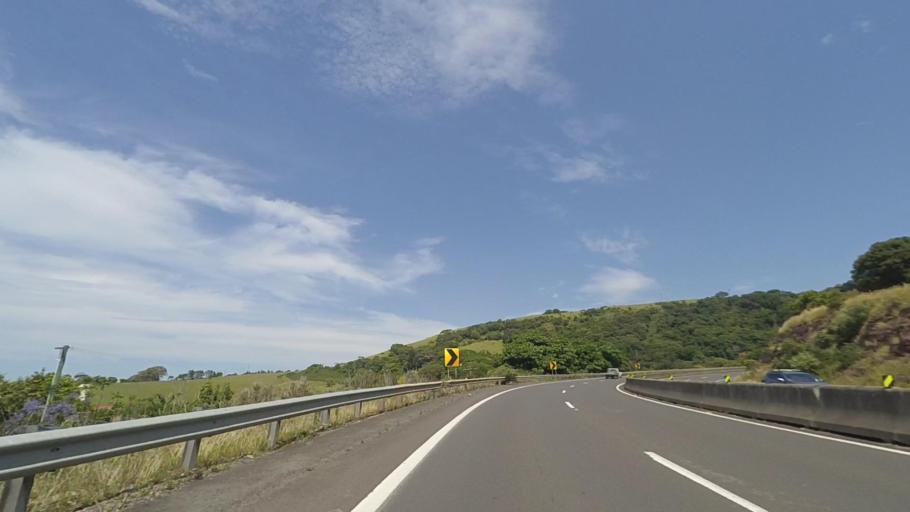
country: AU
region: New South Wales
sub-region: Kiama
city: Kiama
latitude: -34.7001
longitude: 150.8396
